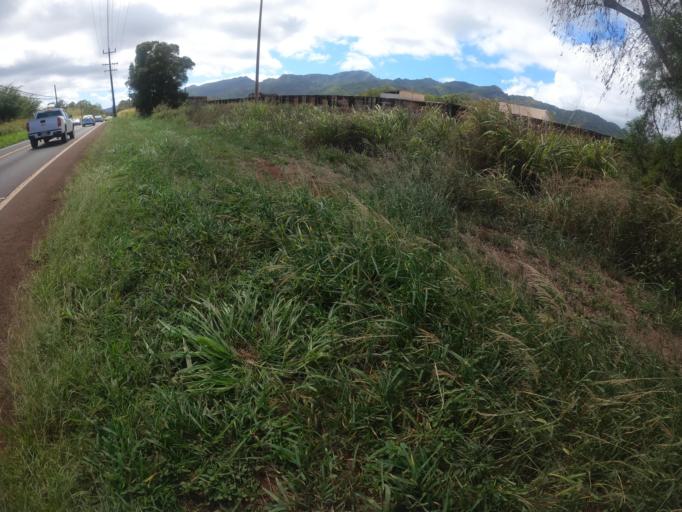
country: US
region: Hawaii
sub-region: Honolulu County
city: Schofield Barracks
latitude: 21.4614
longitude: -158.0566
